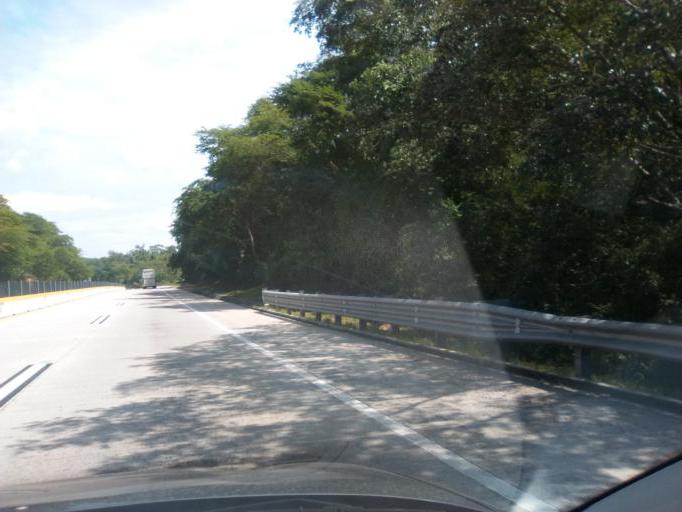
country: MX
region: Guerrero
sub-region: Acapulco de Juarez
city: Colonia Nueva Revolucion
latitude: 16.9293
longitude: -99.7945
